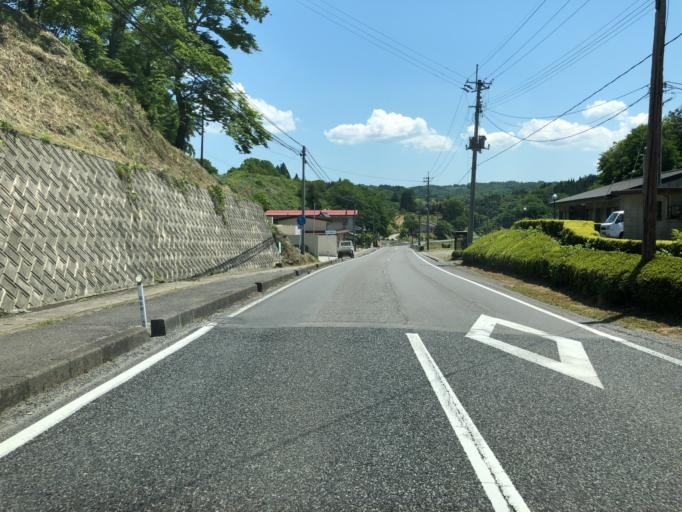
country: JP
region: Fukushima
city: Funehikimachi-funehiki
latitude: 37.4879
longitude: 140.5371
